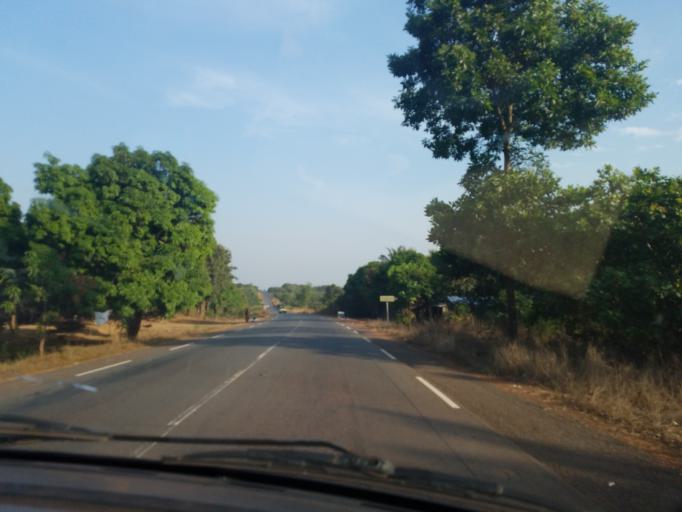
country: GN
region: Boke
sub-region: Boke Prefecture
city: Sangueya
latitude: 10.3766
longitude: -14.3111
